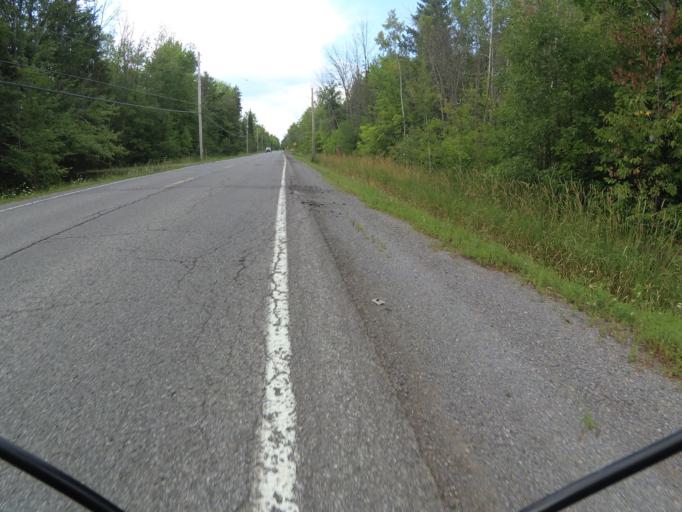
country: CA
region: Ontario
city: Arnprior
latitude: 45.4852
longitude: -76.1061
